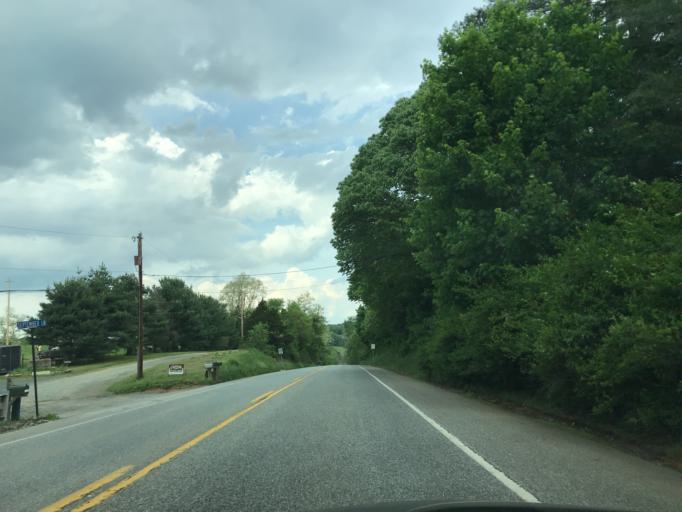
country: US
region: Pennsylvania
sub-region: York County
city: Susquehanna Trails
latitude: 39.7327
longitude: -76.3395
